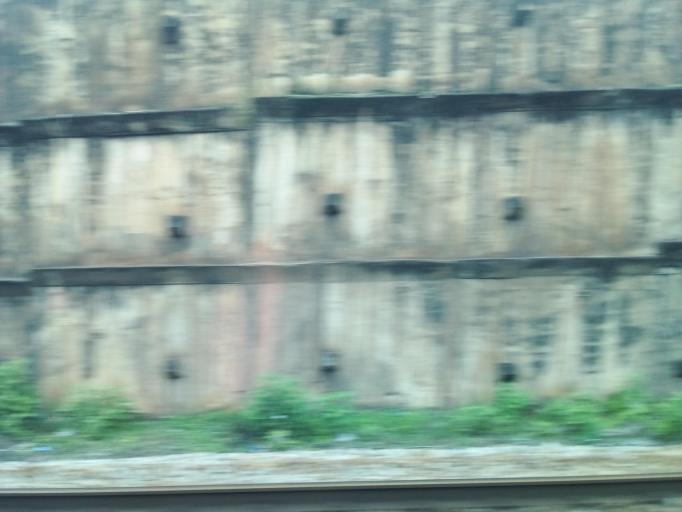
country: BR
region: Minas Gerais
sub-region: Joao Monlevade
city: Joao Monlevade
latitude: -19.8343
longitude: -43.1291
